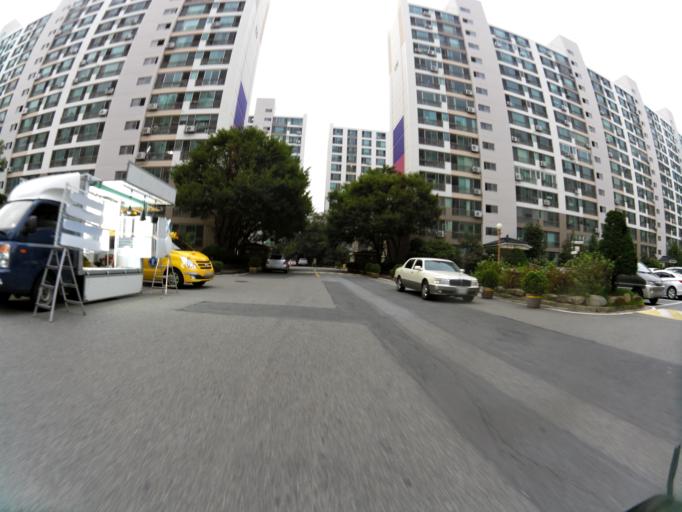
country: KR
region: Daegu
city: Daegu
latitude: 35.8759
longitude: 128.6655
